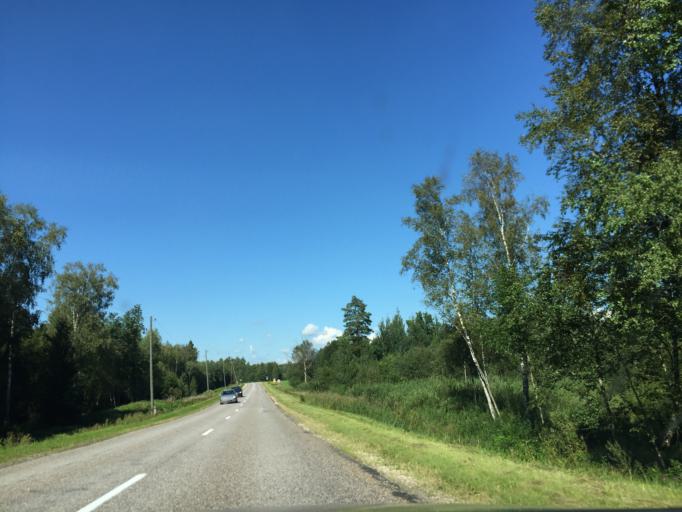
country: LV
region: Limbazu Rajons
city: Limbazi
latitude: 57.4699
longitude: 24.7119
